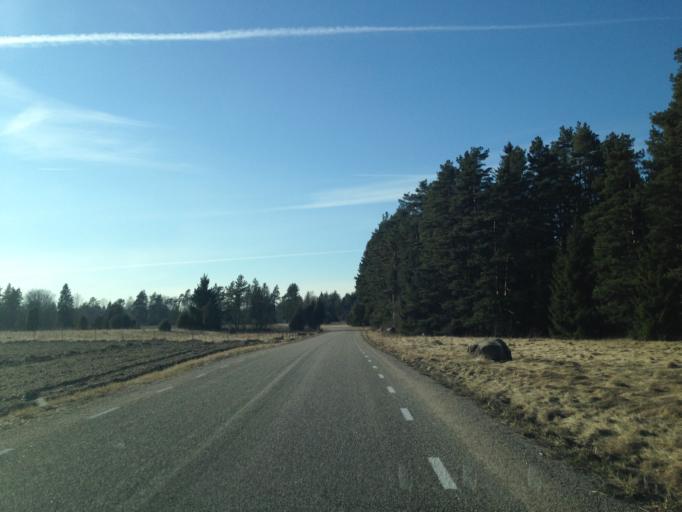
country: EE
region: Harju
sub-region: Nissi vald
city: Turba
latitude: 59.1411
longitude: 24.1643
